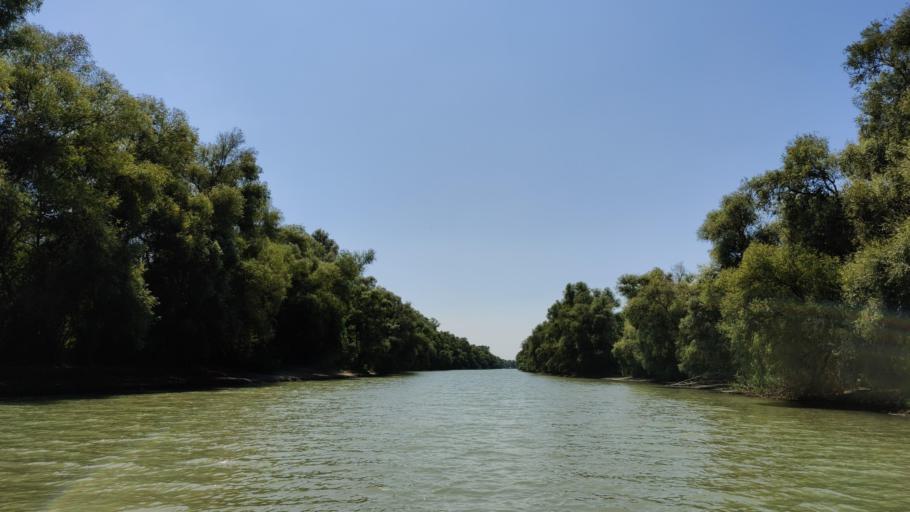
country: RO
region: Tulcea
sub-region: Comuna Pardina
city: Pardina
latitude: 45.2528
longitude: 28.9259
